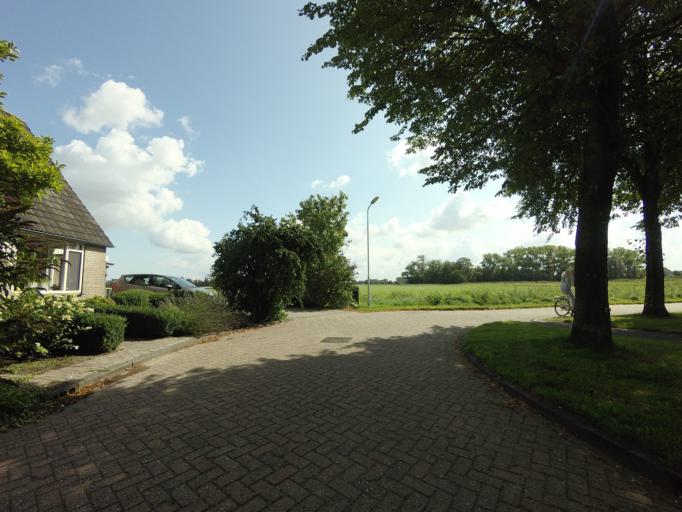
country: NL
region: Friesland
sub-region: Gemeente Het Bildt
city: Sint Annaparochie
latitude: 53.2804
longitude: 5.6654
